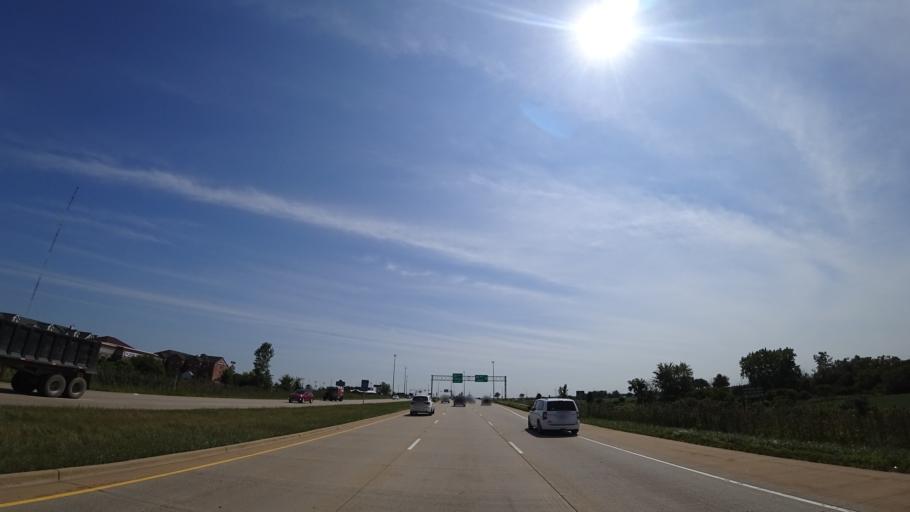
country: US
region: Illinois
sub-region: Cook County
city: Orland Hills
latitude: 41.5584
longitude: -87.8534
